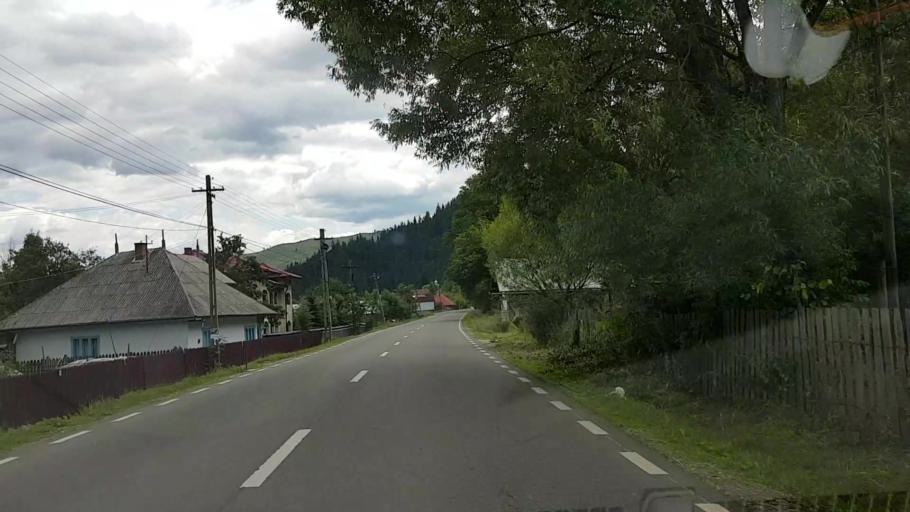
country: RO
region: Neamt
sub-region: Comuna Borca
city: Borca
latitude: 47.1882
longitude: 25.7734
